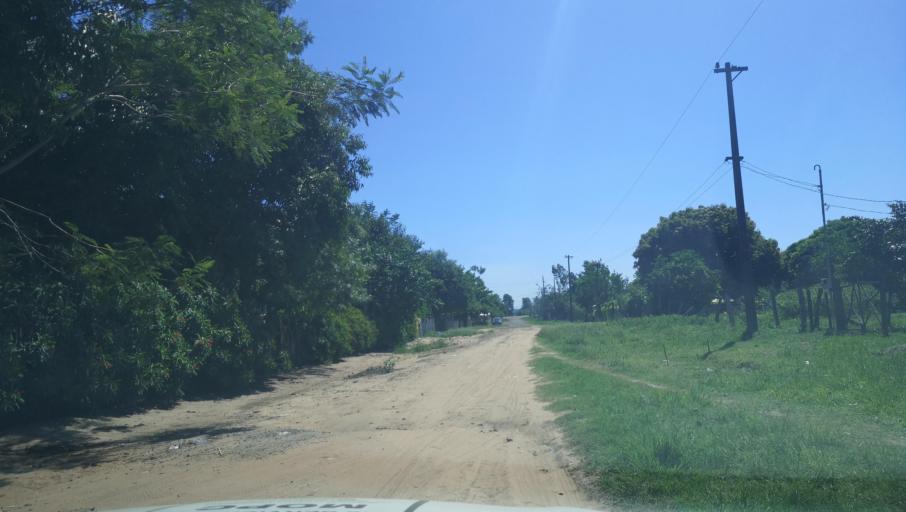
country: PY
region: Caaguazu
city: Carayao
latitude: -25.2036
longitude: -56.3955
